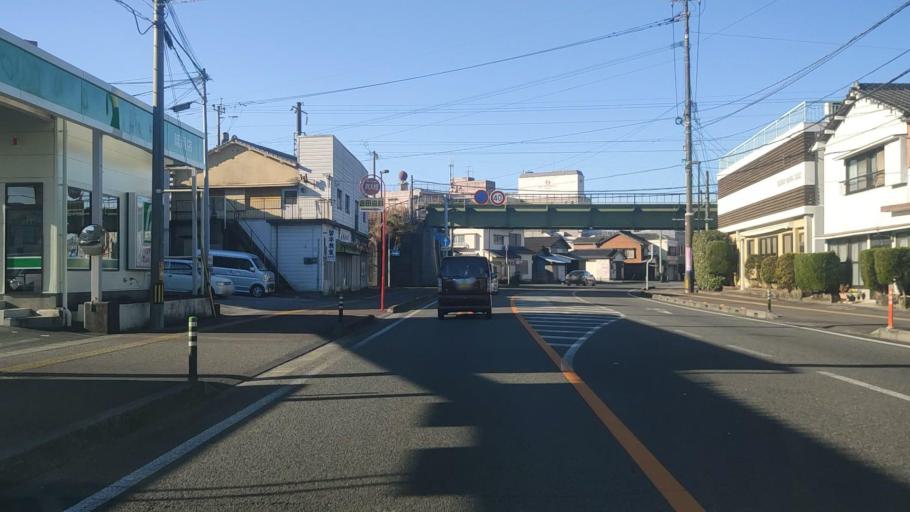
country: JP
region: Miyazaki
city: Nobeoka
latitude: 32.5856
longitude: 131.6744
